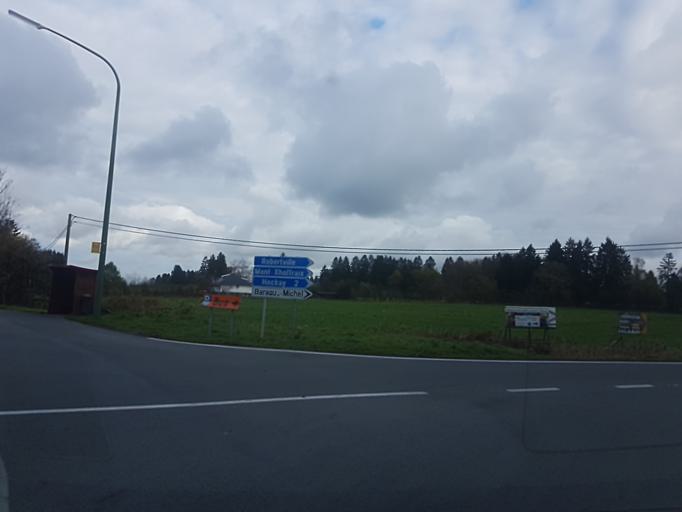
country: BE
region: Wallonia
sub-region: Province de Liege
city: Jalhay
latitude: 50.4801
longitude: 5.9645
